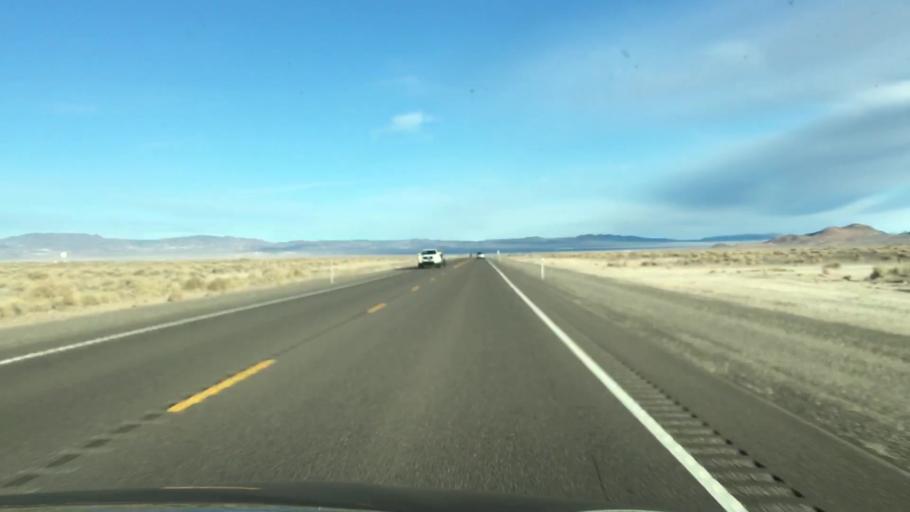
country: US
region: Nevada
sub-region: Nye County
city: Tonopah
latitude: 38.1294
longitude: -117.5630
